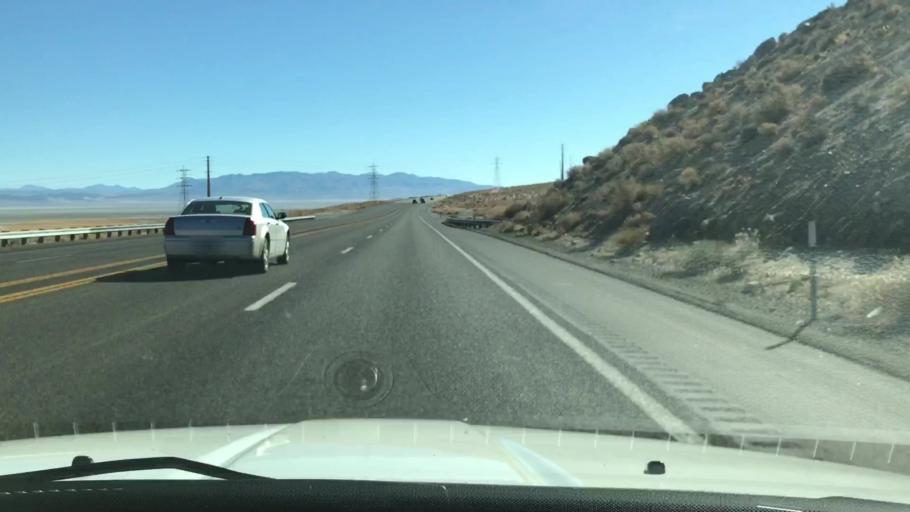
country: US
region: California
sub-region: Inyo County
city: Lone Pine
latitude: 36.5139
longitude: -118.0359
